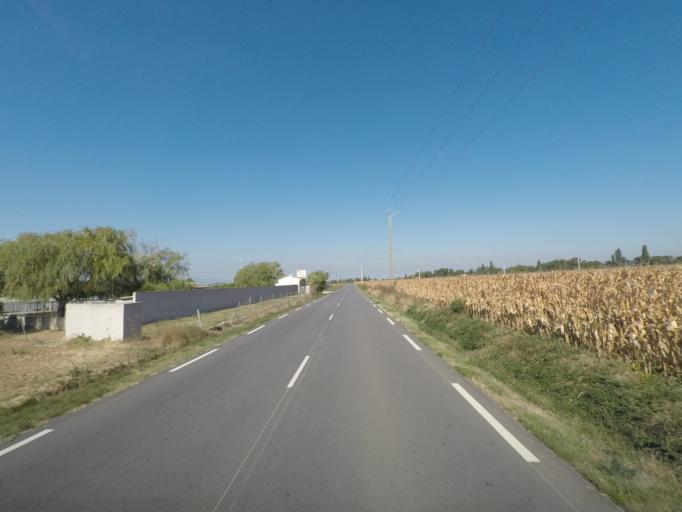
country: FR
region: Rhone-Alpes
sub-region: Departement de la Drome
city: Upie
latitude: 44.8022
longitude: 5.0156
